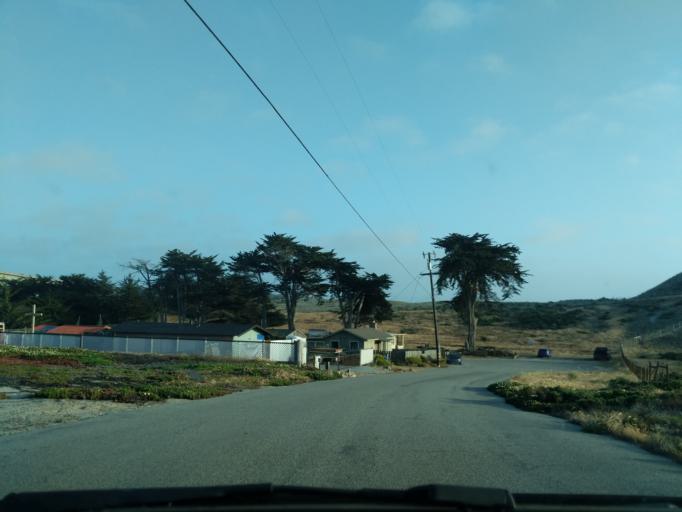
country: US
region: California
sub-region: Monterey County
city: Marina
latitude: 36.6811
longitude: -121.8090
